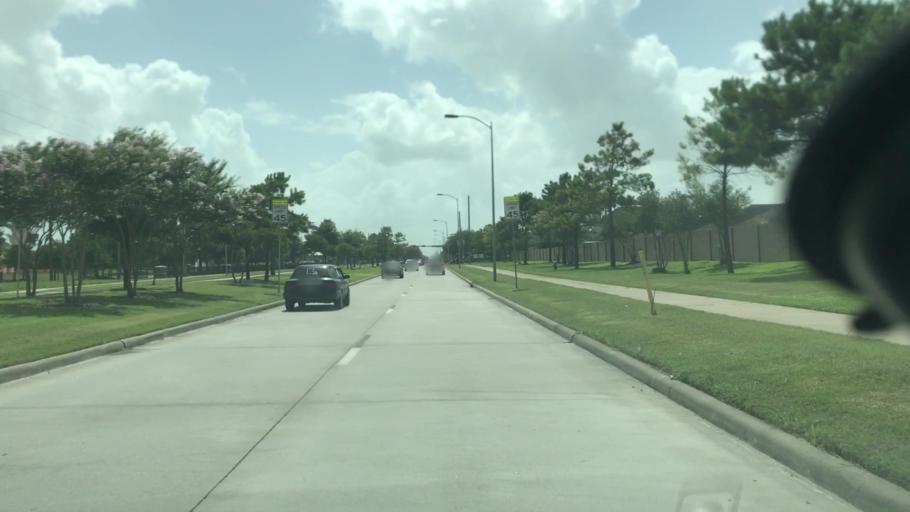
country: US
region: Texas
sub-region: Fort Bend County
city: Fresno
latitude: 29.5557
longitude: -95.4041
